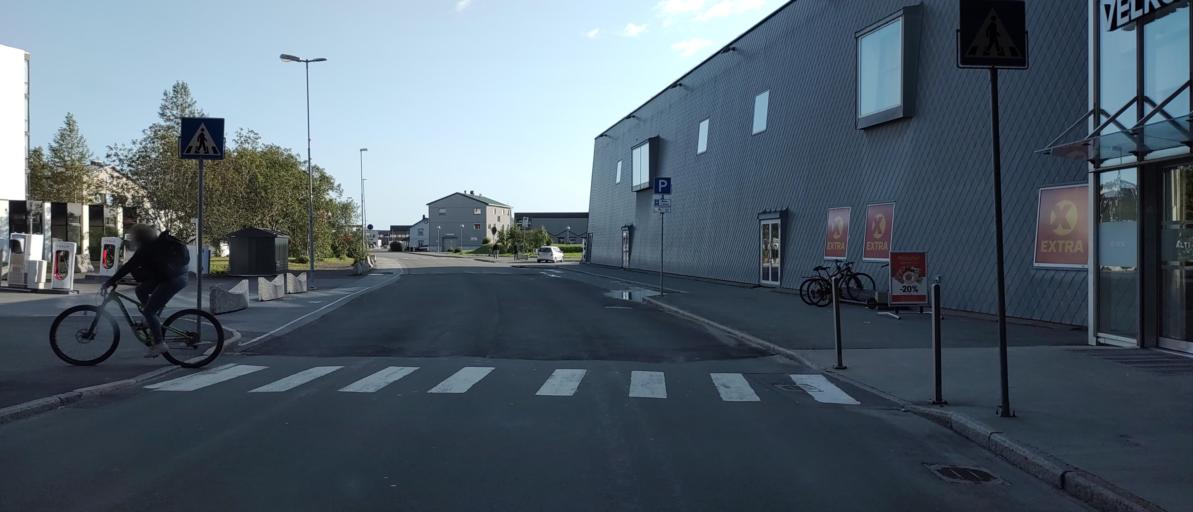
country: NO
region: Nordland
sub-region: Vagan
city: Svolvaer
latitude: 68.2335
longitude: 14.5594
